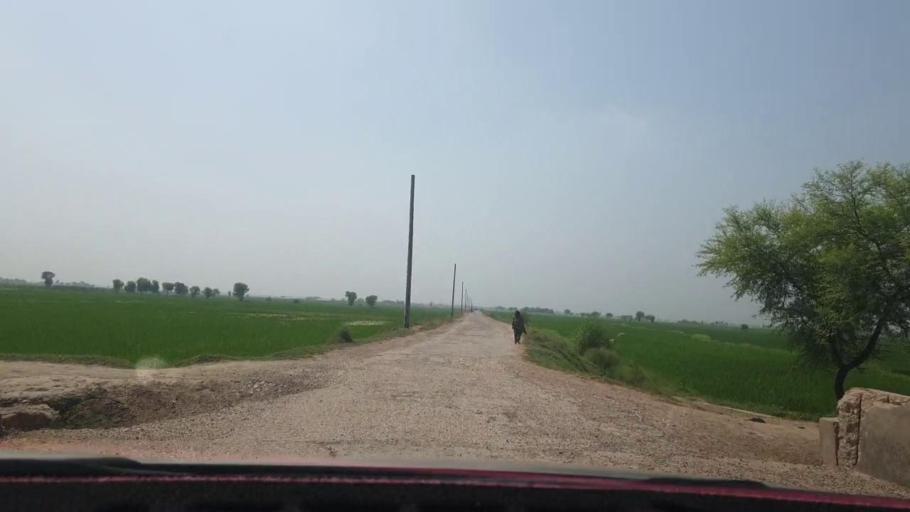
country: PK
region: Sindh
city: Warah
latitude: 27.4148
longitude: 67.8444
